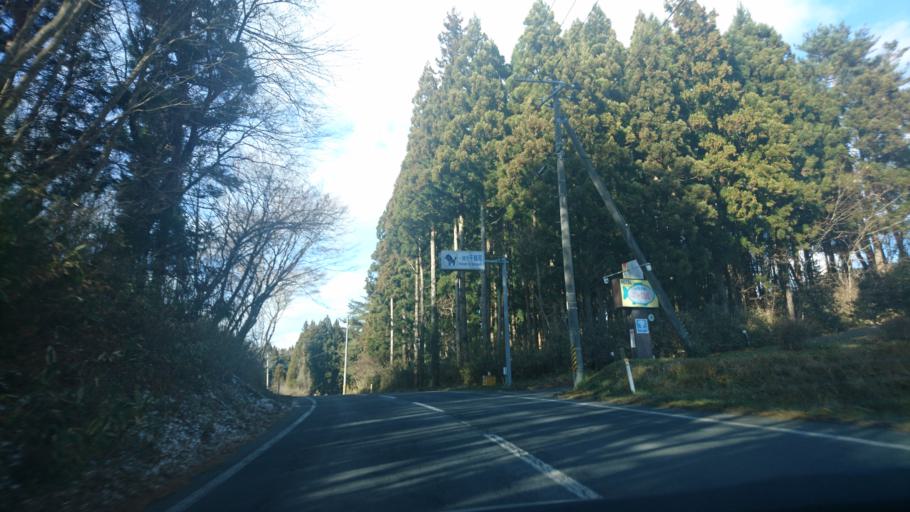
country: JP
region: Iwate
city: Ichinoseki
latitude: 38.9413
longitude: 141.4100
